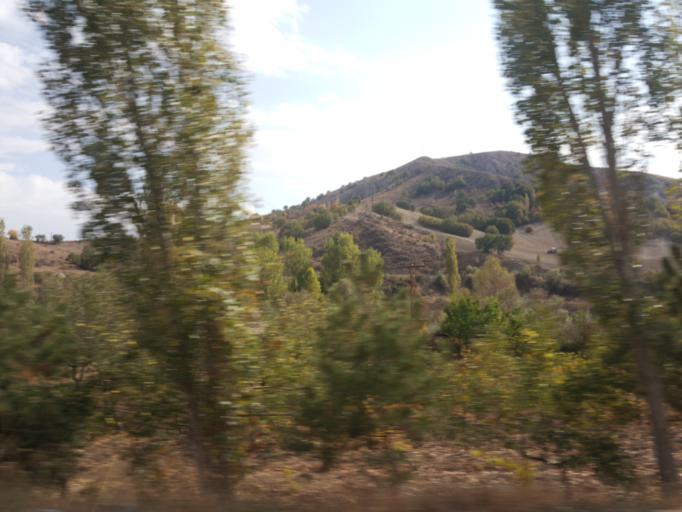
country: TR
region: Corum
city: Sungurlu
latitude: 40.2039
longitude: 34.5246
